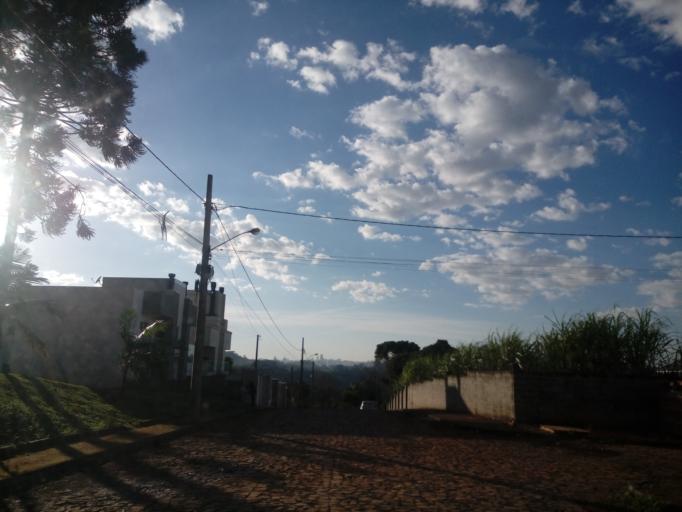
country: BR
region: Santa Catarina
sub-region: Chapeco
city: Chapeco
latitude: -27.1074
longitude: -52.6695
